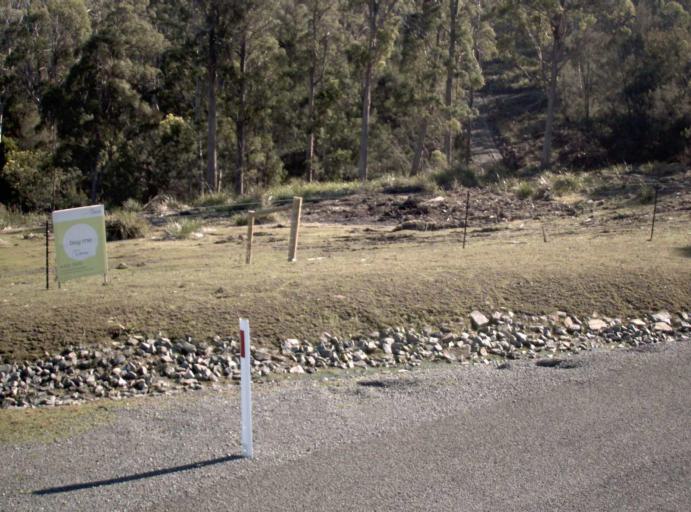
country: AU
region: Tasmania
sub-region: Launceston
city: Mayfield
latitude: -41.2803
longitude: 147.0277
